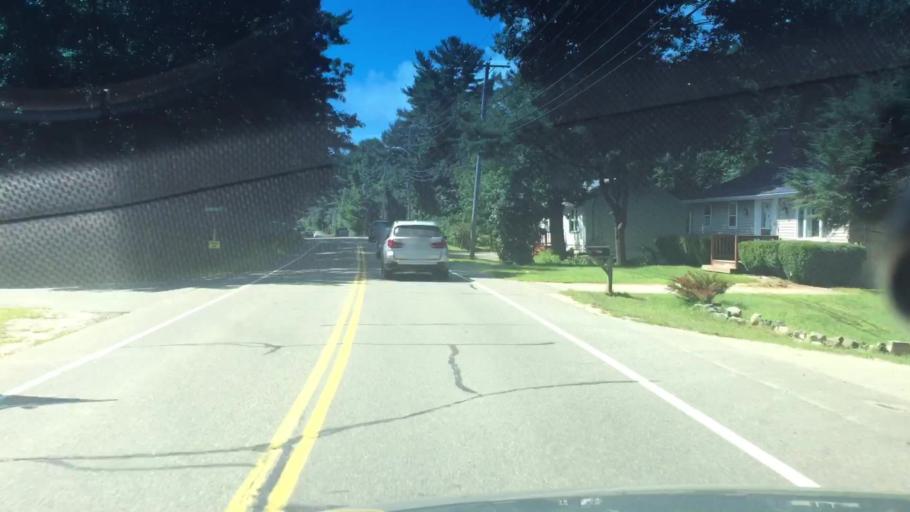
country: US
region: Maine
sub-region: York County
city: York Beach
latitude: 43.1657
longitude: -70.6247
